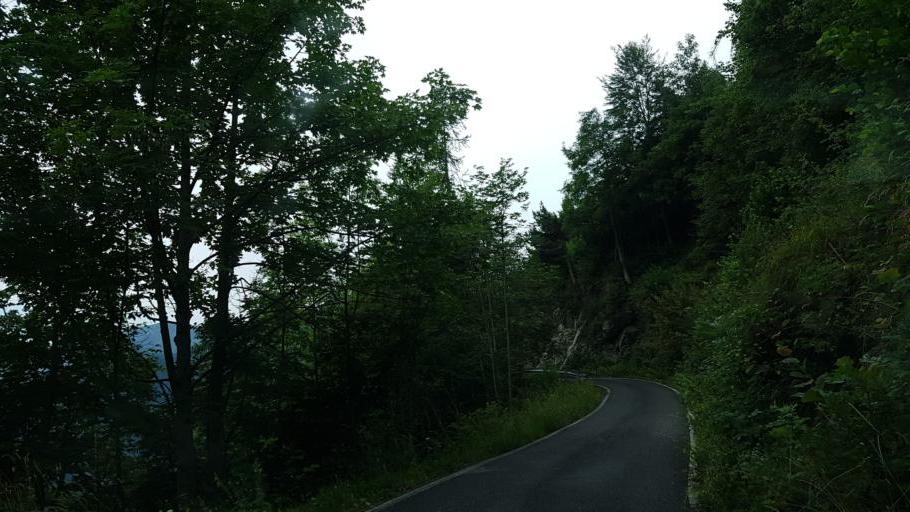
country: IT
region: Piedmont
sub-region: Provincia di Cuneo
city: Stroppo
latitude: 44.5185
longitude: 7.1159
